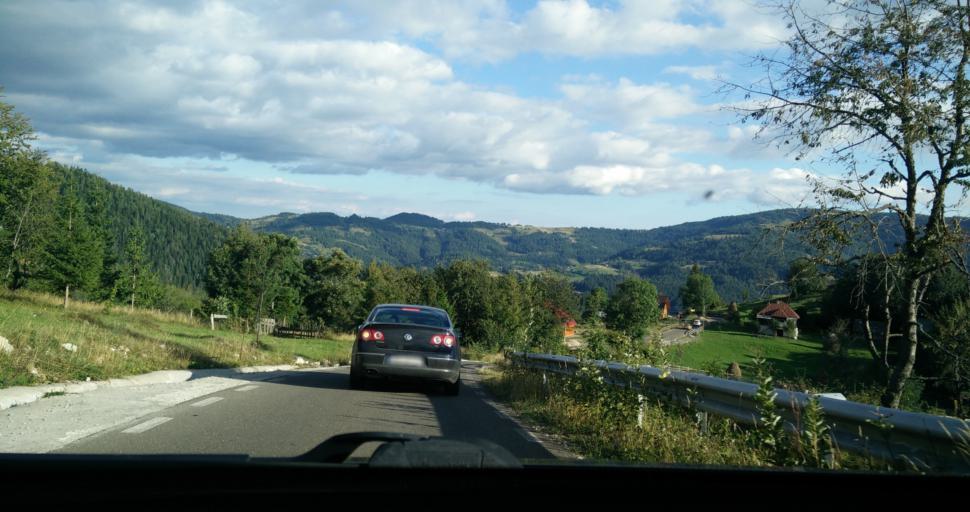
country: RO
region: Alba
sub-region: Comuna Scarisoara
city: Scarisoara
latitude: 46.4724
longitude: 22.8313
